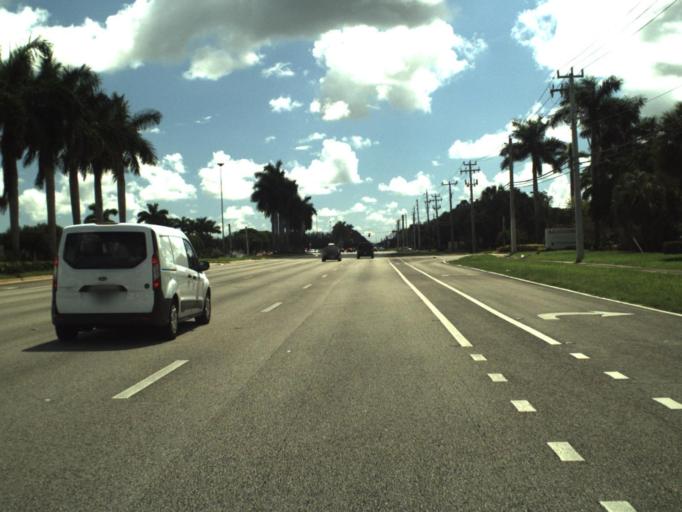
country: US
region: Florida
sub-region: Broward County
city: Sunshine Ranches
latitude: 26.0076
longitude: -80.3320
